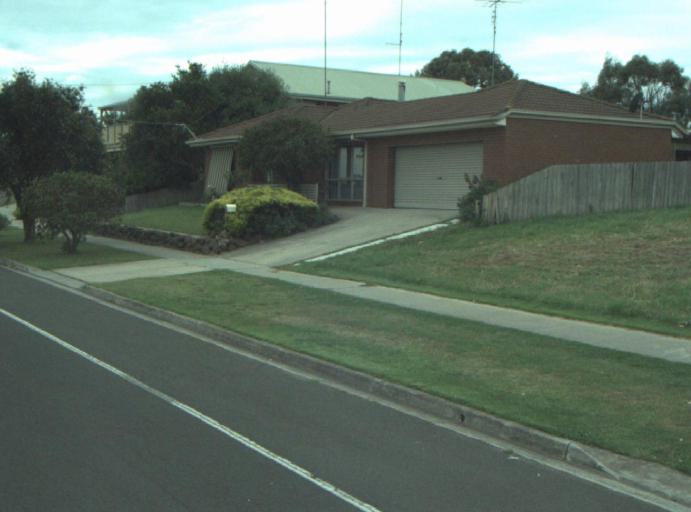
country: AU
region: Victoria
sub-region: Greater Geelong
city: Leopold
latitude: -38.1812
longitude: 144.4629
